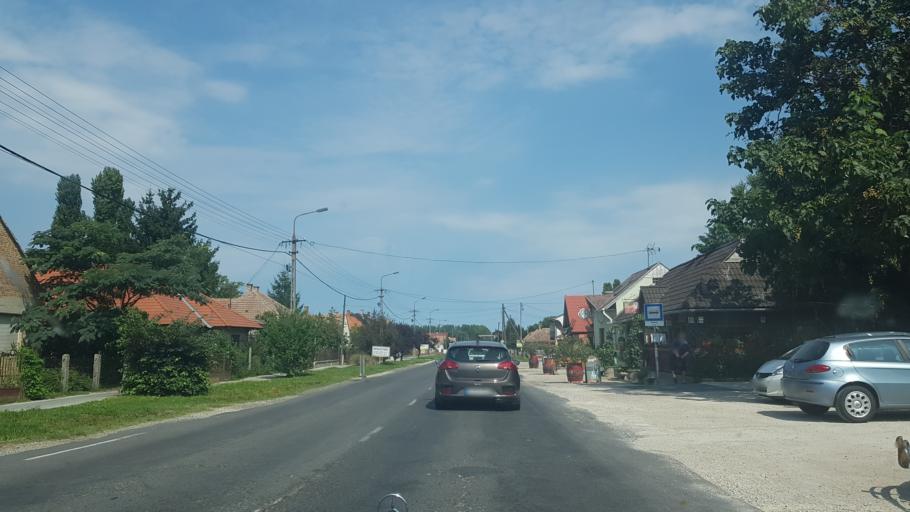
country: HU
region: Somogy
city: Kethely
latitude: 46.6509
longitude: 17.3925
